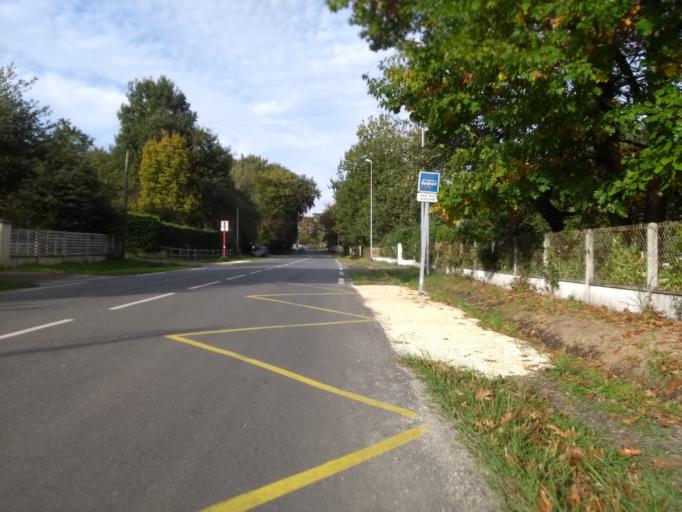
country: FR
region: Aquitaine
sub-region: Departement de la Gironde
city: Canejan
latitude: 44.7825
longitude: -0.6633
